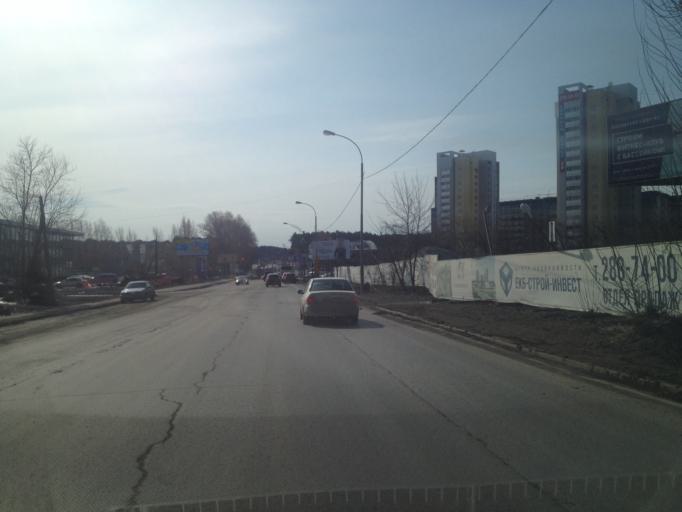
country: RU
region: Sverdlovsk
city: Yekaterinburg
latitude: 56.7998
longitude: 60.5947
